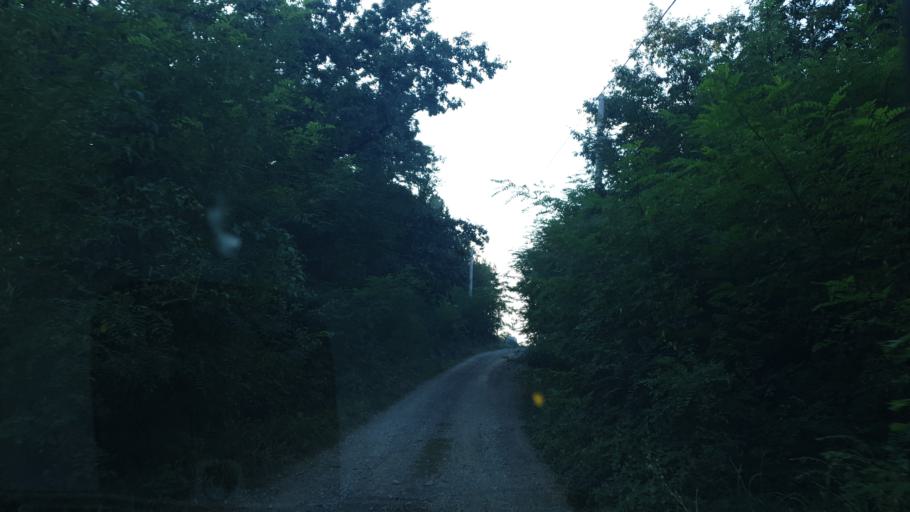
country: RS
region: Central Serbia
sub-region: Zlatiborski Okrug
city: Kosjeric
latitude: 44.0025
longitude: 20.0012
